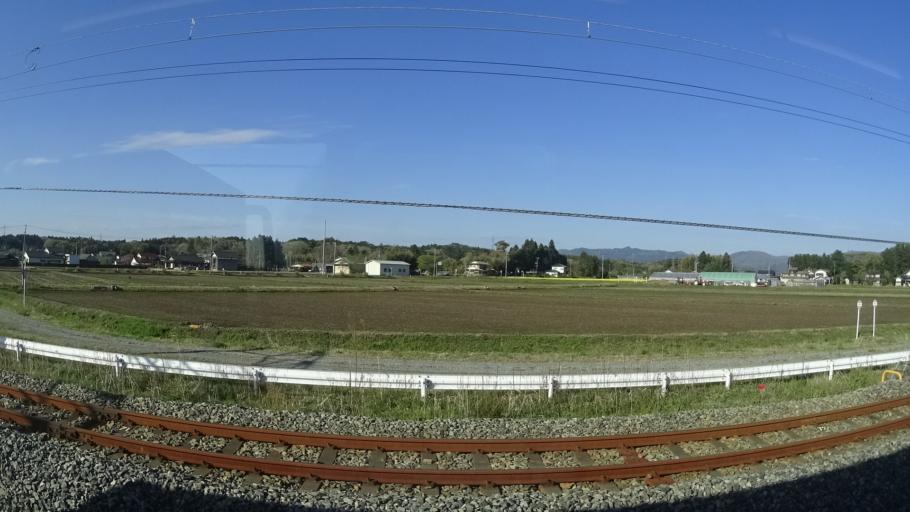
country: JP
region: Fukushima
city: Namie
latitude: 37.6066
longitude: 140.9896
